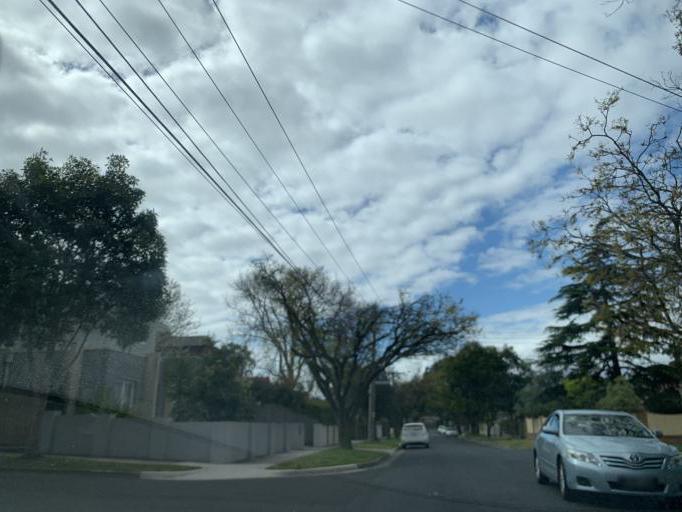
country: AU
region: Victoria
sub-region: Bayside
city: Cheltenham
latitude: -37.9754
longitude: 145.0491
